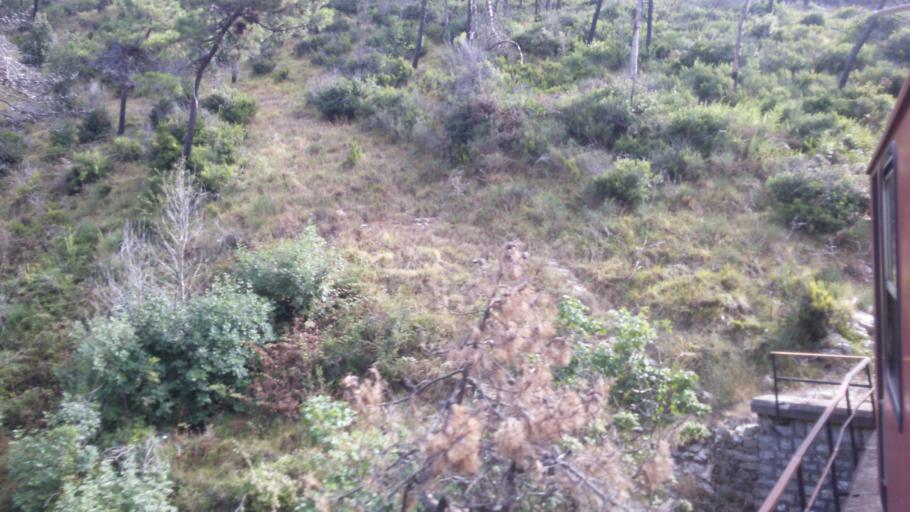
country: IT
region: Liguria
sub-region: Provincia di Genova
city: Genoa
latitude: 44.4405
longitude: 8.9390
